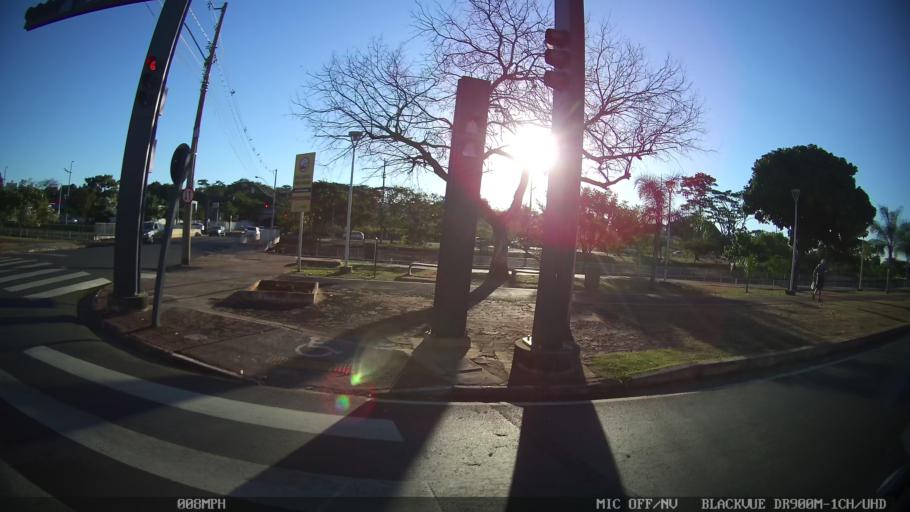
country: BR
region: Sao Paulo
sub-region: Sao Jose Do Rio Preto
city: Sao Jose do Rio Preto
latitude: -20.7960
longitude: -49.3761
